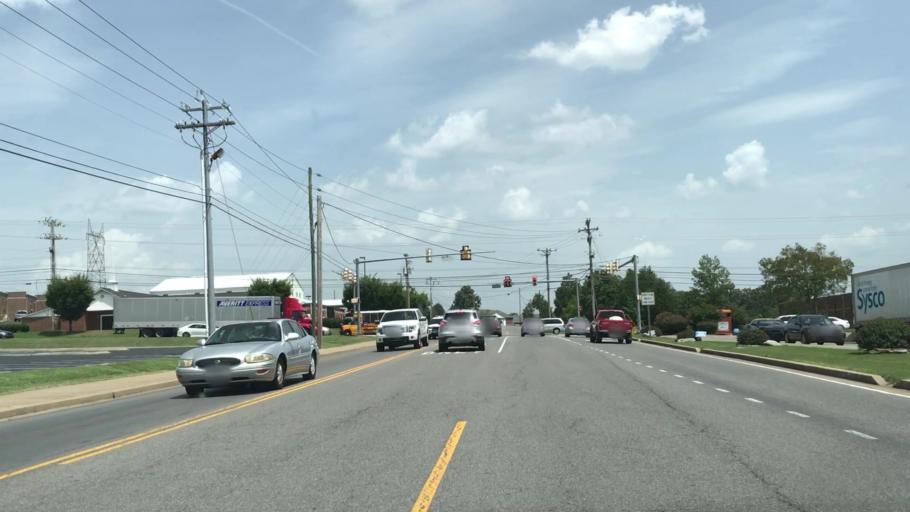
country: US
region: Tennessee
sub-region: Rutherford County
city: Smyrna
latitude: 35.9842
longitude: -86.5476
